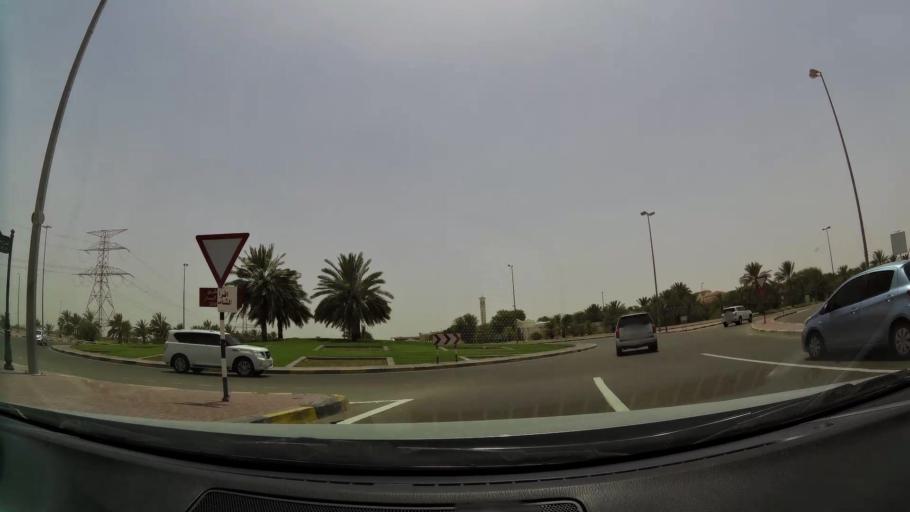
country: AE
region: Abu Dhabi
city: Al Ain
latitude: 24.1849
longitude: 55.6797
